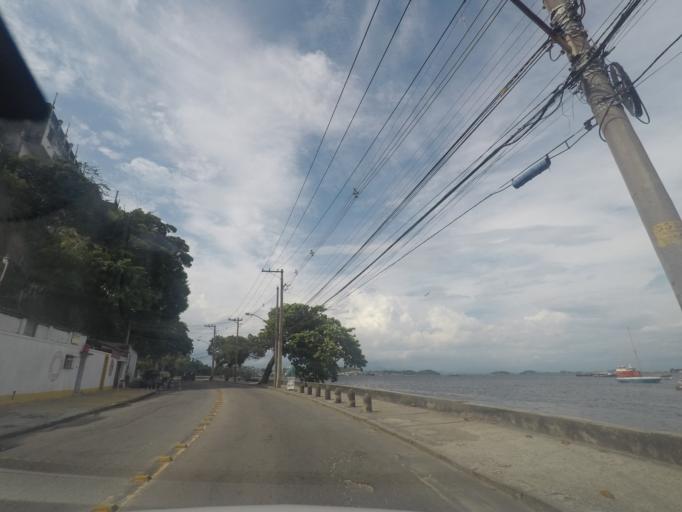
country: BR
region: Rio de Janeiro
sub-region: Rio De Janeiro
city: Rio de Janeiro
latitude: -22.8185
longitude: -43.1750
